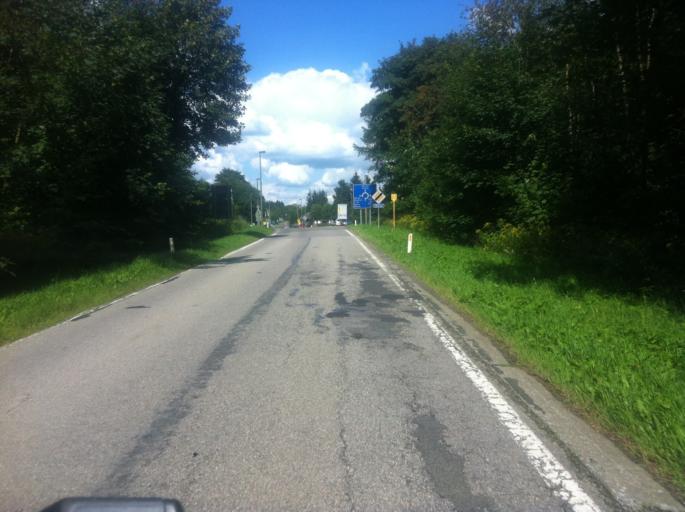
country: DE
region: Rheinland-Pfalz
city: Scheid
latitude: 50.3780
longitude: 6.3412
